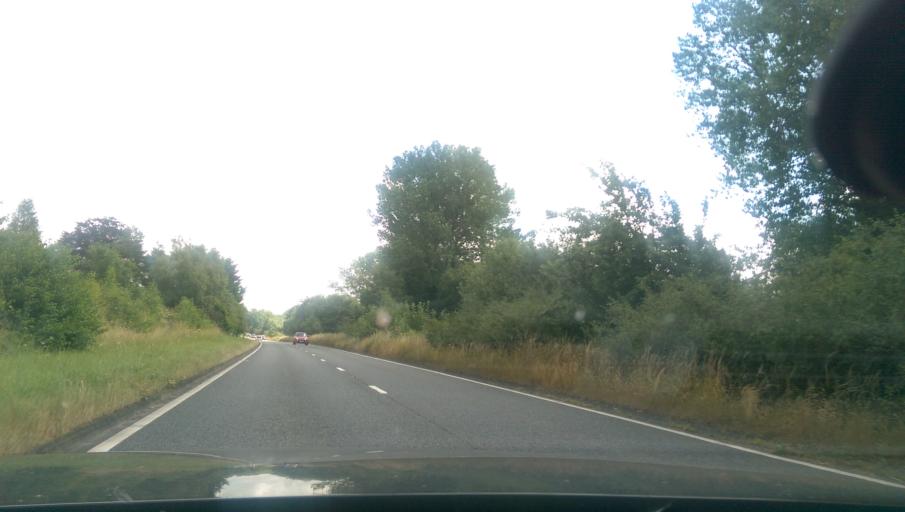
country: GB
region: England
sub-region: Wiltshire
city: Stapleford
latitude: 51.1325
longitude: -1.9192
